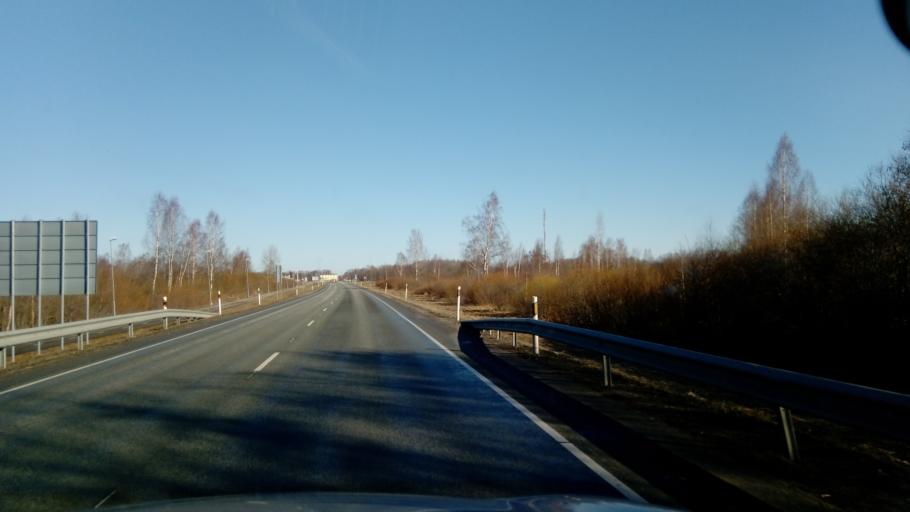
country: EE
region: Laeaene-Virumaa
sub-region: Rakvere linn
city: Rakvere
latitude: 59.3427
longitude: 26.3419
